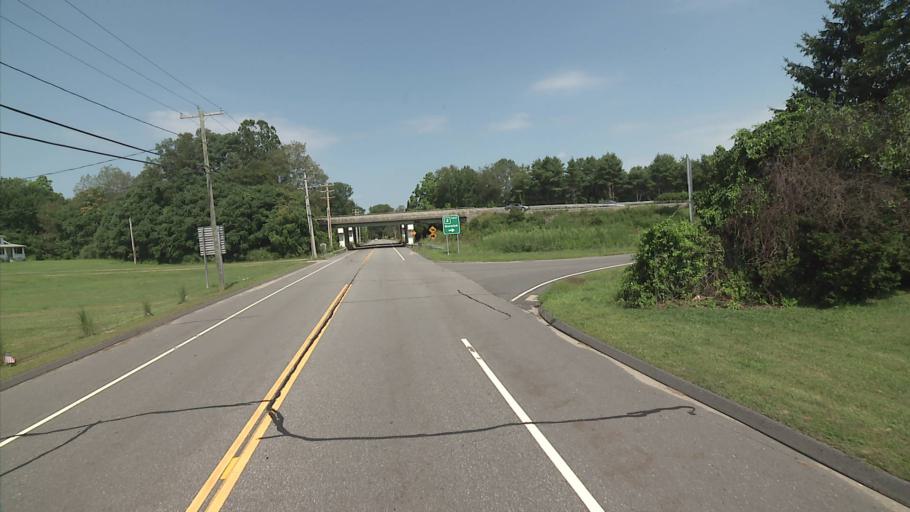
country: US
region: Connecticut
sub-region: New London County
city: Norwich
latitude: 41.5648
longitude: -72.1425
